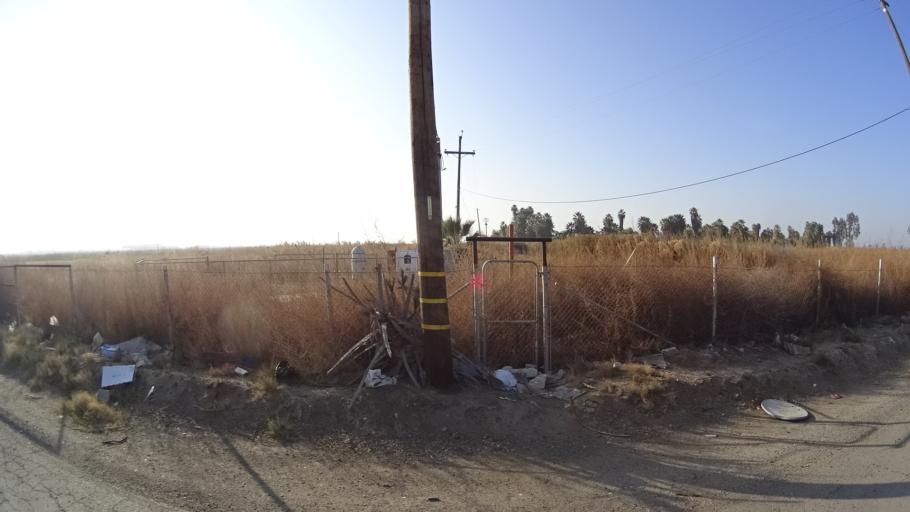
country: US
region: California
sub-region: Kern County
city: Greenfield
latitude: 35.2379
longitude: -118.9807
